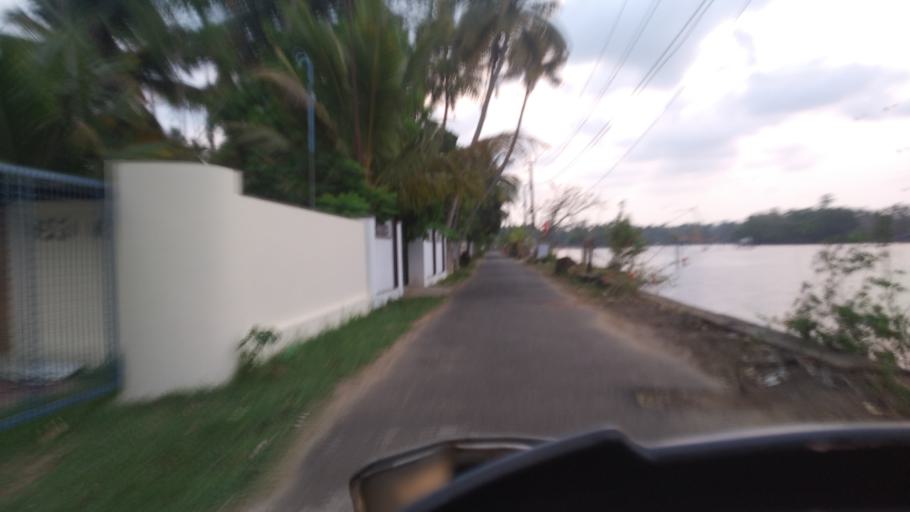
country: IN
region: Kerala
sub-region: Thrissur District
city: Kodungallur
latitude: 10.1443
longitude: 76.2055
